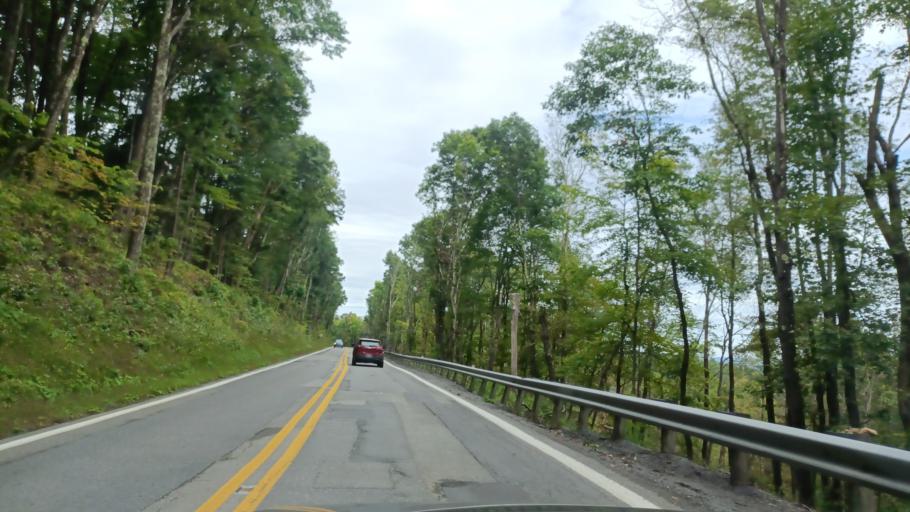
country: US
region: West Virginia
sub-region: Preston County
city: Kingwood
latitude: 39.3271
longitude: -79.7527
